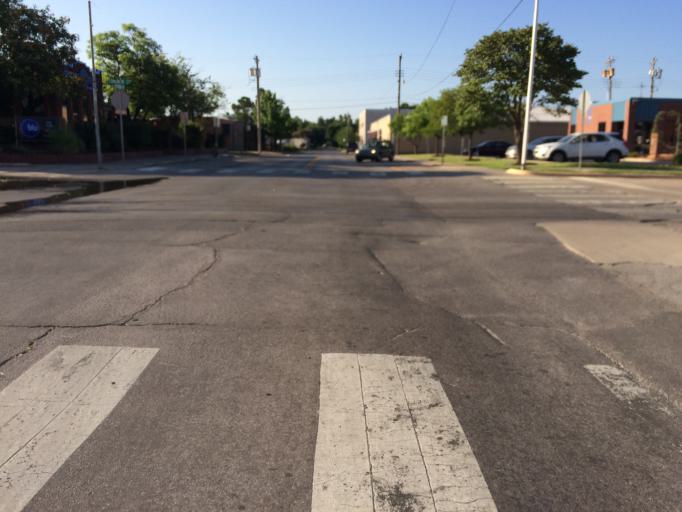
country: US
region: Oklahoma
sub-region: Cleveland County
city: Norman
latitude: 35.2213
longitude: -97.4400
